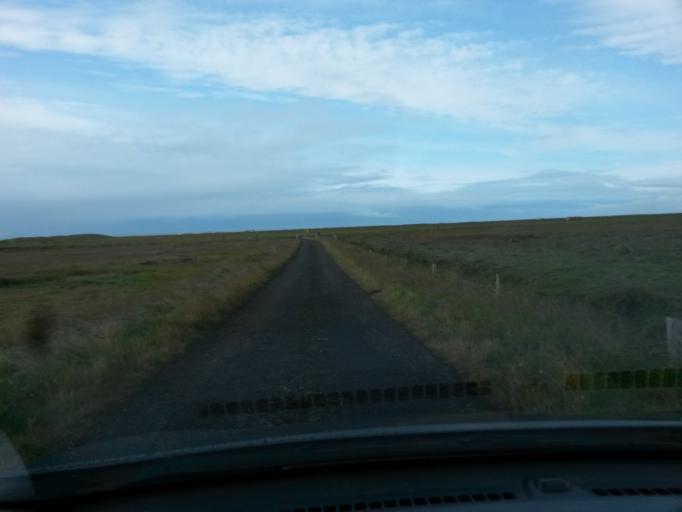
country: IS
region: South
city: Vestmannaeyjar
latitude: 63.4376
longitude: -19.1914
